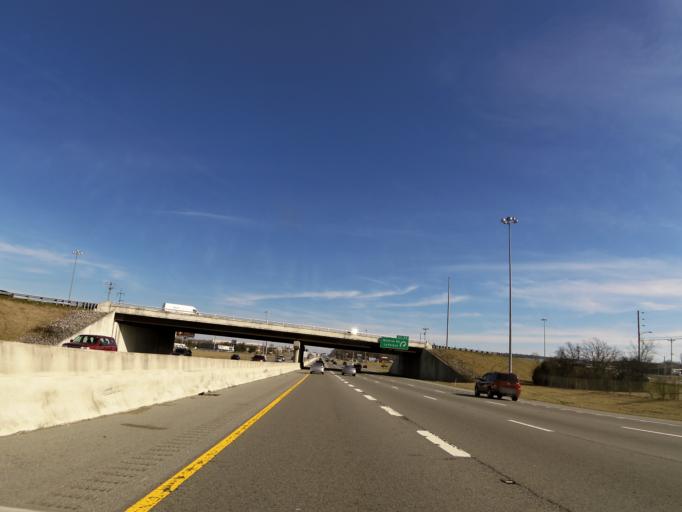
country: US
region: Tennessee
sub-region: Rutherford County
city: La Vergne
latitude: 35.9960
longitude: -86.5978
